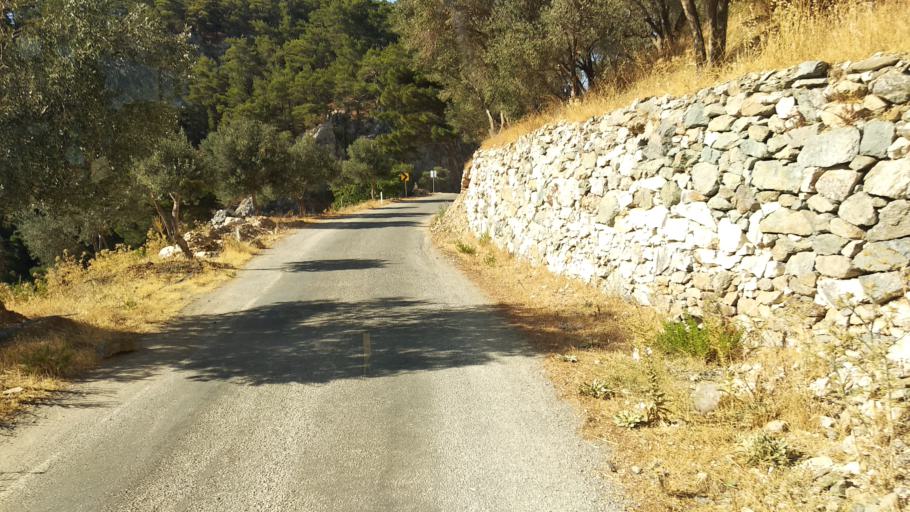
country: TR
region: Izmir
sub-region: Seferihisar
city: Seferhisar
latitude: 38.3204
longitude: 26.9572
